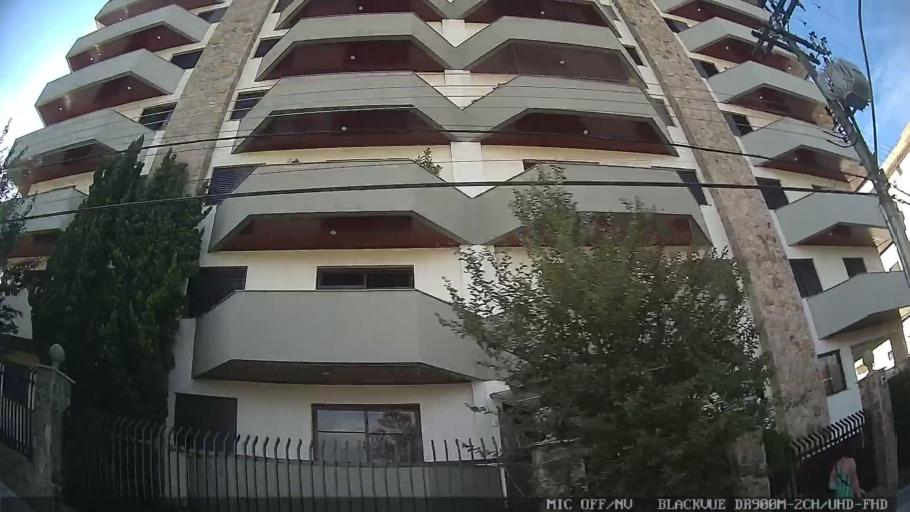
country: BR
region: Sao Paulo
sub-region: Serra Negra
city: Serra Negra
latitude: -22.6170
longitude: -46.7029
